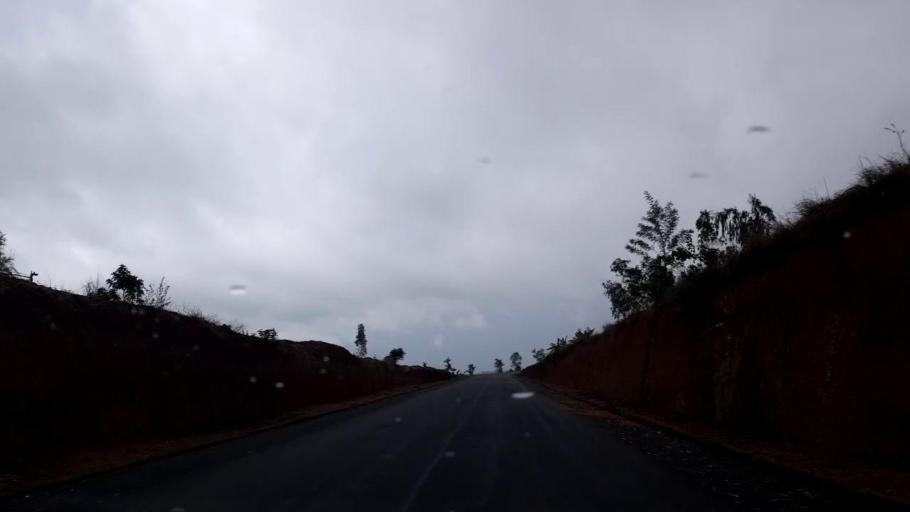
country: RW
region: Northern Province
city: Byumba
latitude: -1.4264
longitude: 30.2664
